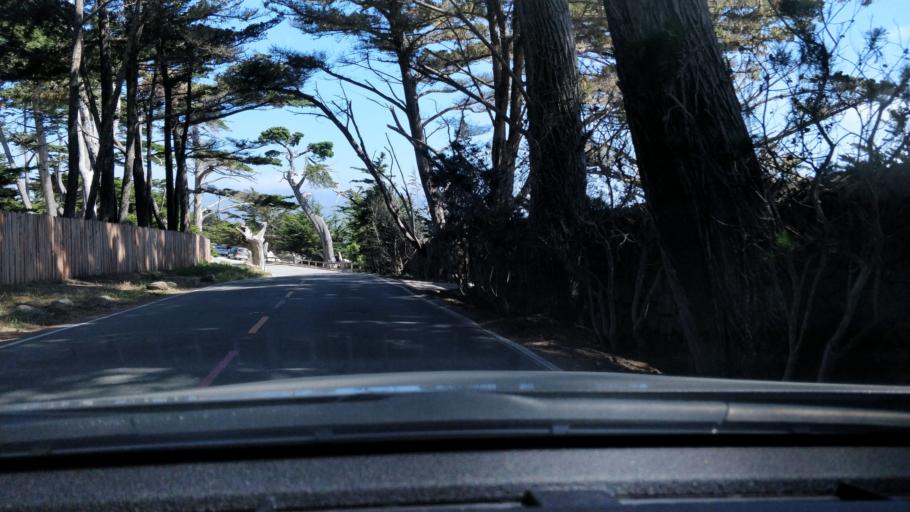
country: US
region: California
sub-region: Monterey County
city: Del Monte Forest
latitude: 36.5633
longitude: -121.9558
